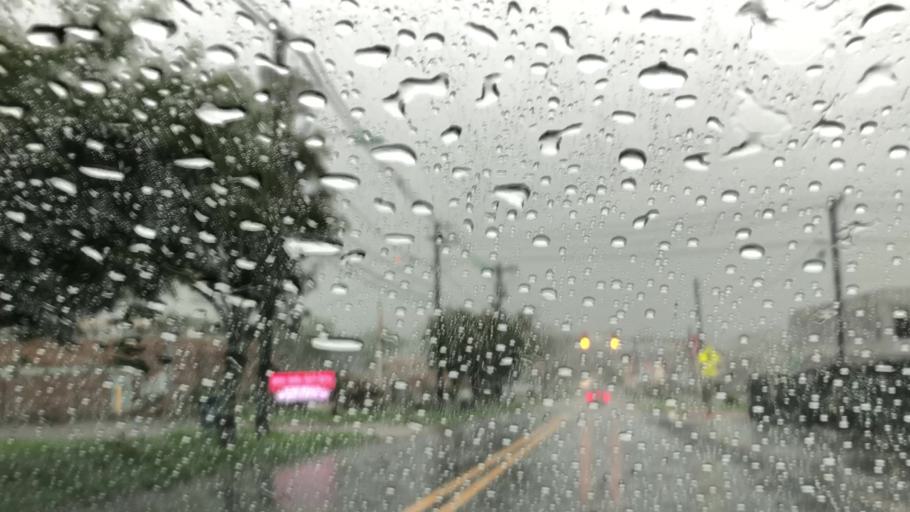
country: US
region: New Jersey
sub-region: Bergen County
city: Saddle Brook
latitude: 40.8956
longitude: -74.0836
